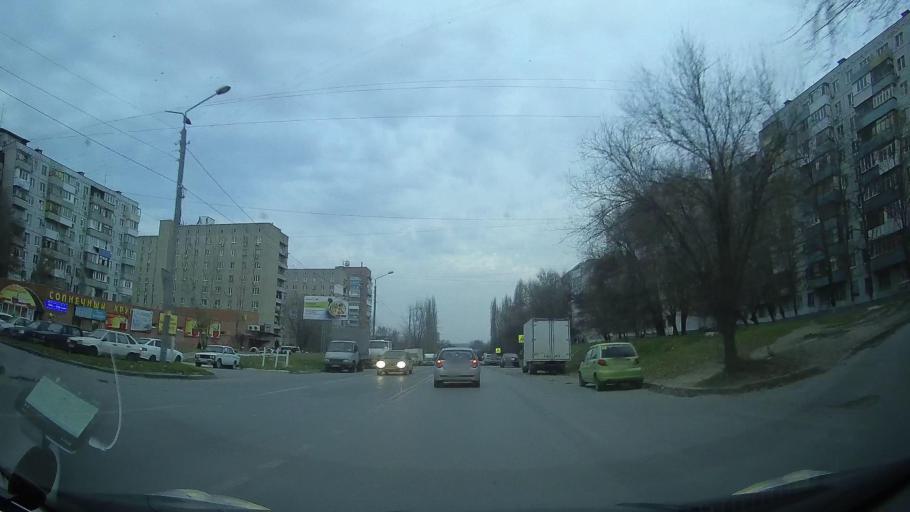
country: RU
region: Rostov
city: Severnyy
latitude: 47.3009
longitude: 39.7230
